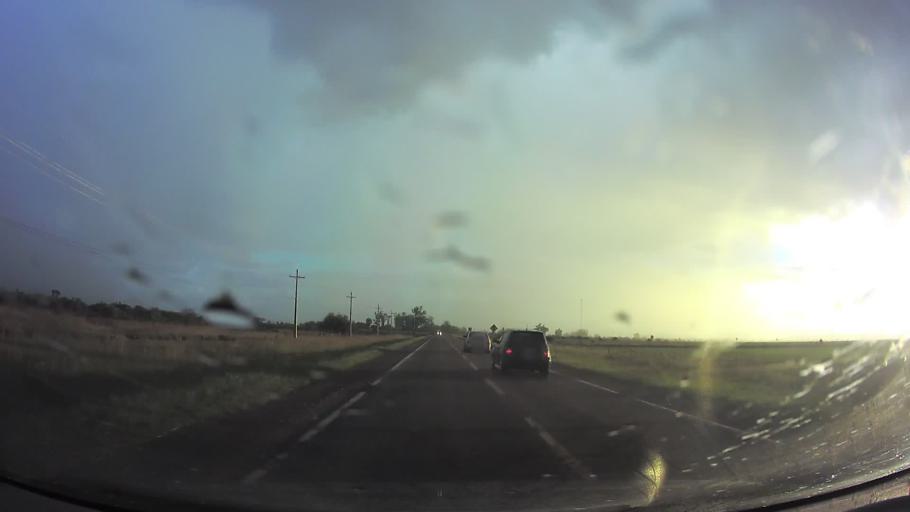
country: PY
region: Paraguari
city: Paraguari
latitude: -25.6865
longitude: -57.1681
